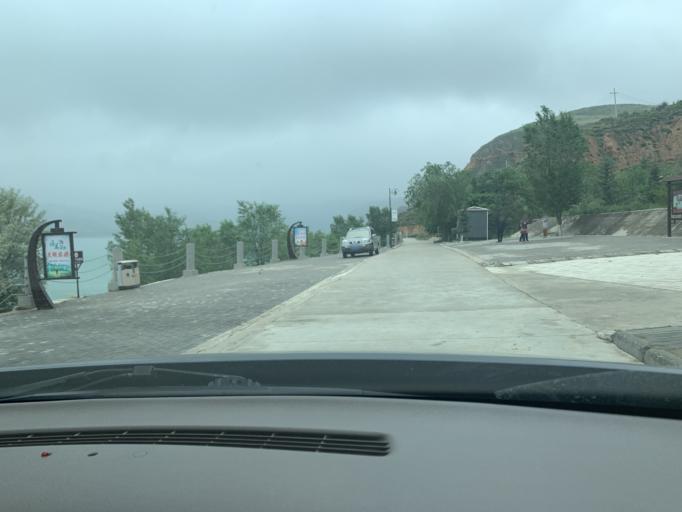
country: CN
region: Gansu Sheng
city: Gulang
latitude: 37.5632
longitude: 102.7426
